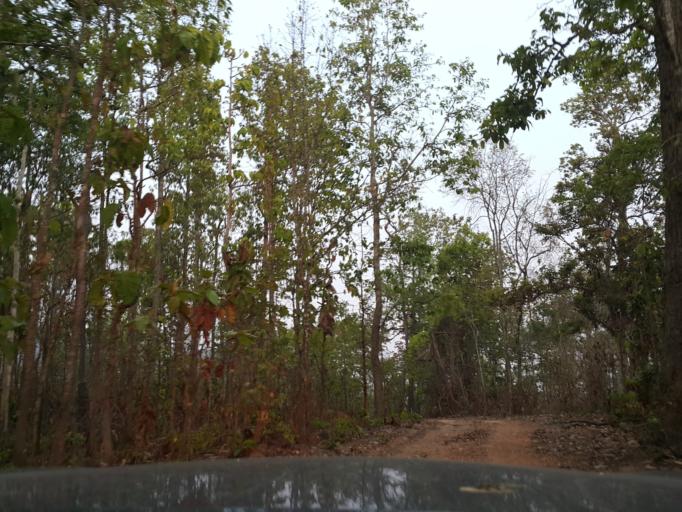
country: TH
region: Lamphun
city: Thung Hua Chang
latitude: 17.9123
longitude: 99.0774
